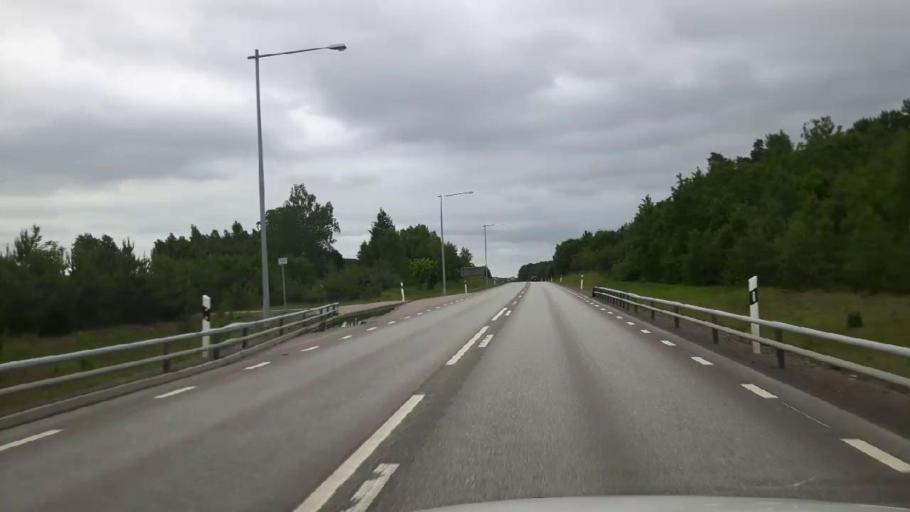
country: SE
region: Vaestmanland
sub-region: Kopings Kommun
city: Koping
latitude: 59.5428
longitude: 15.9338
